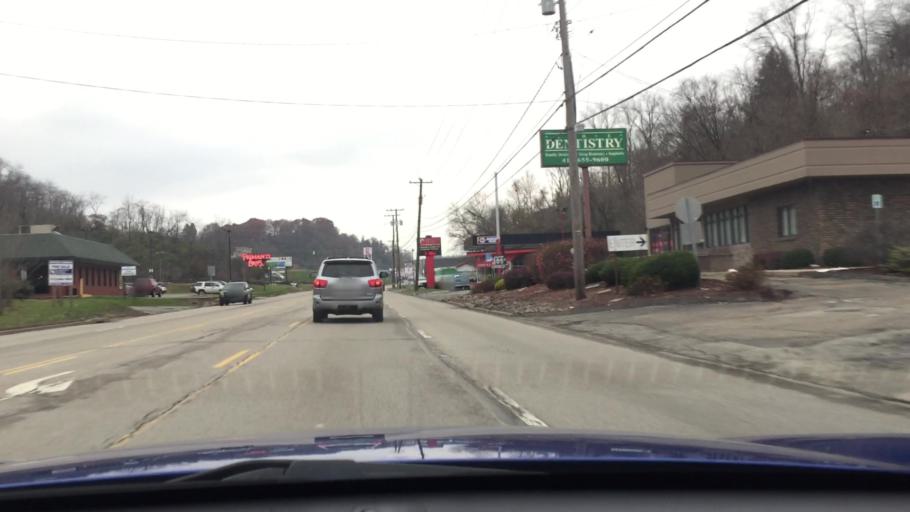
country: US
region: Pennsylvania
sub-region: Allegheny County
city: Pleasant Hills
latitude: 40.3234
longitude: -79.9431
